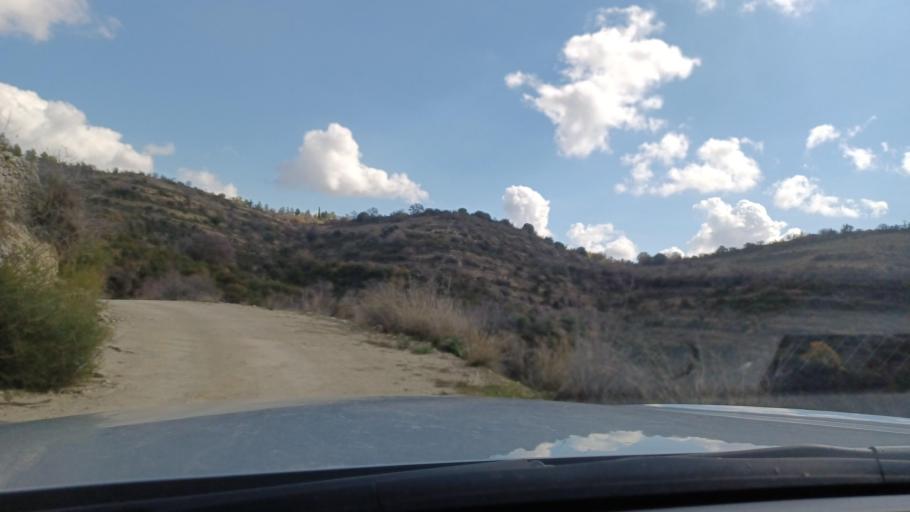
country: CY
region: Limassol
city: Pachna
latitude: 34.8332
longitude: 32.7650
